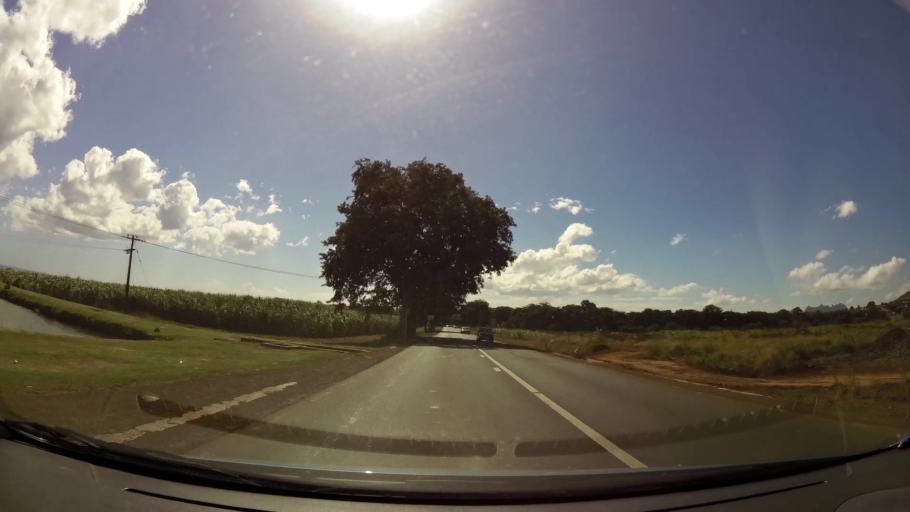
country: MU
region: Black River
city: Cascavelle
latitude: -20.2667
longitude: 57.4067
